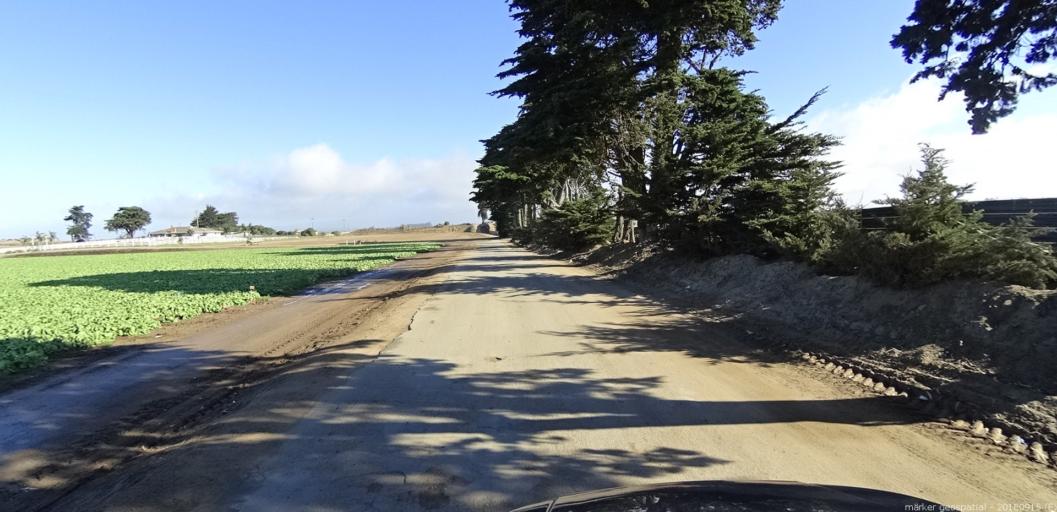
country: US
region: California
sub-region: Monterey County
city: Elkhorn
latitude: 36.8273
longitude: -121.7892
